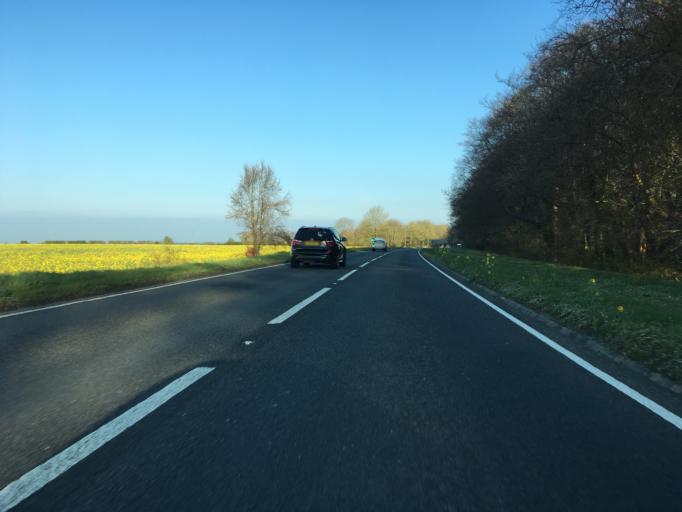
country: GB
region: England
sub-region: Gloucestershire
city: Bourton on the Water
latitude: 51.8159
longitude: -1.7501
